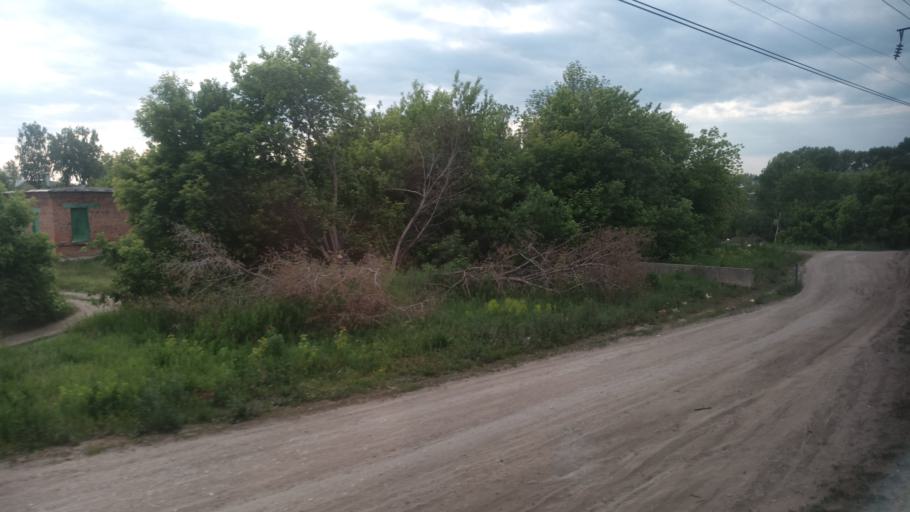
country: RU
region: Altai Krai
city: Novoaltaysk
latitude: 53.4161
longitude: 83.9160
